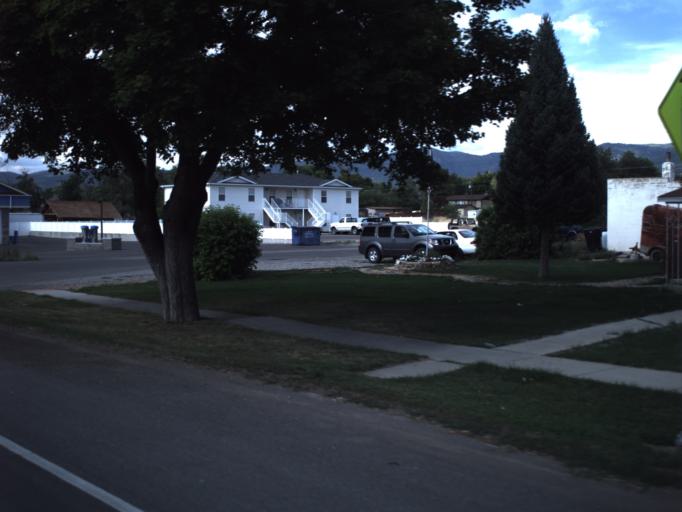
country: US
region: Utah
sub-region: Sanpete County
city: Mount Pleasant
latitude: 39.5376
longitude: -111.4552
